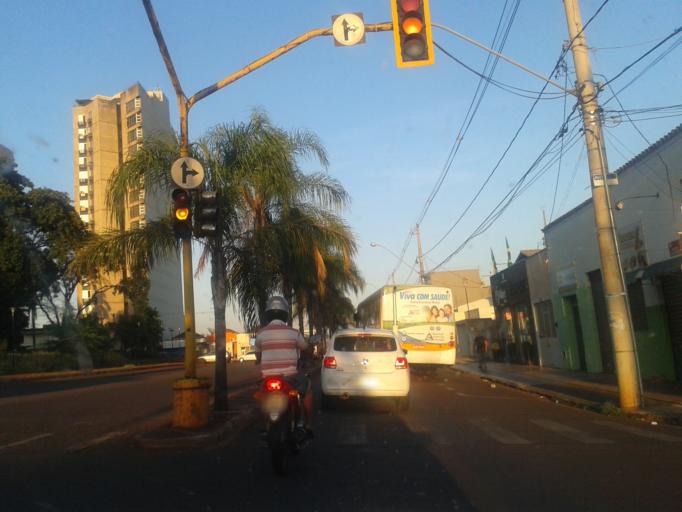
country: BR
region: Minas Gerais
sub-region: Ituiutaba
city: Ituiutaba
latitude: -18.9745
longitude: -49.4601
